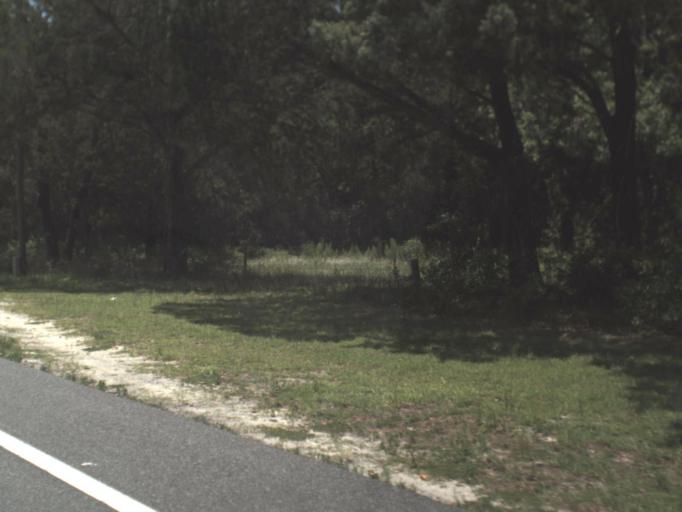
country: US
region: Florida
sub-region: Lafayette County
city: Mayo
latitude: 29.8908
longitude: -82.9547
